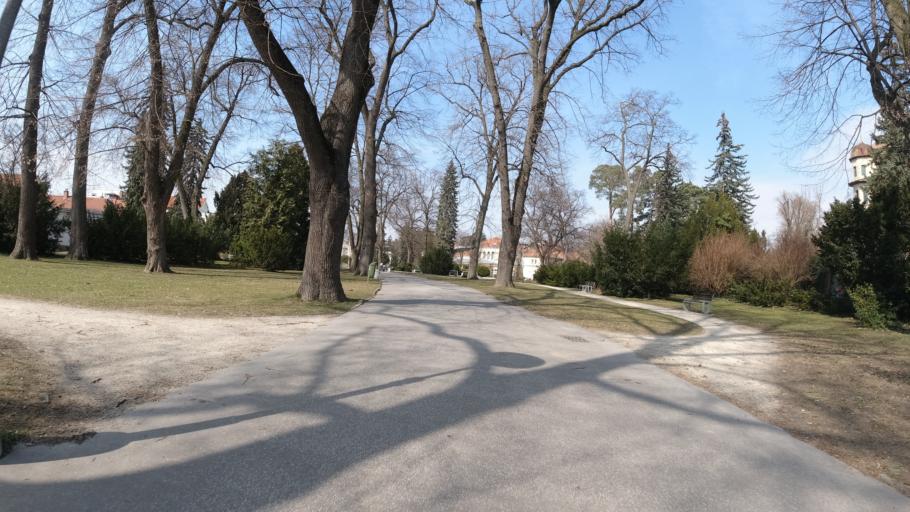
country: SK
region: Trnavsky
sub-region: Okres Trnava
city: Piestany
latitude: 48.5895
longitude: 17.8381
